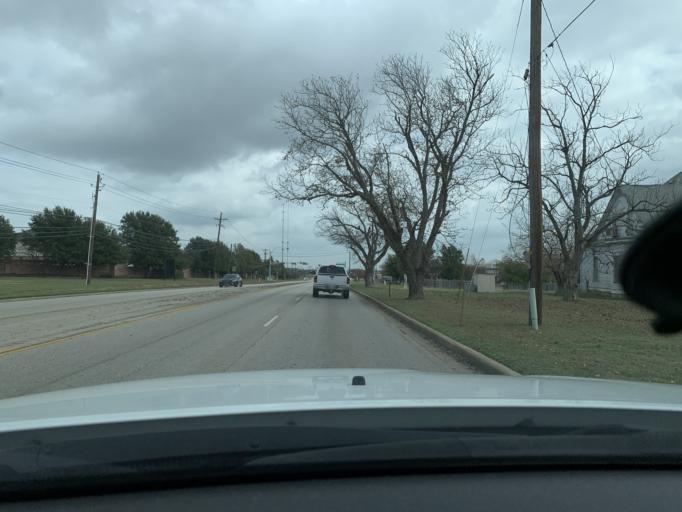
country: US
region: Texas
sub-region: Williamson County
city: Round Rock
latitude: 30.5666
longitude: -97.6665
